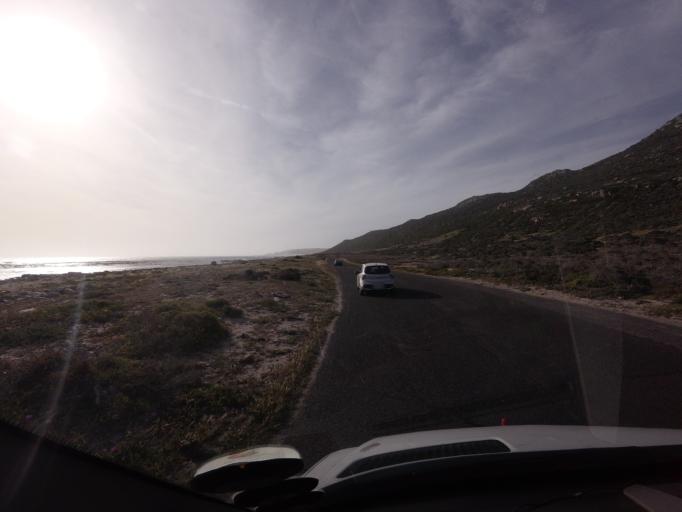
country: ZA
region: Western Cape
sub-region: City of Cape Town
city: Retreat
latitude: -34.3521
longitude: 18.4711
